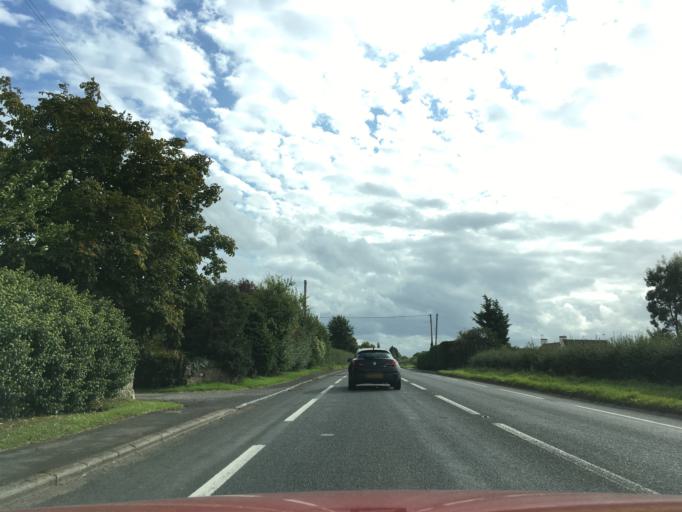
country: GB
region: England
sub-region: South Gloucestershire
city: Falfield
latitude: 51.6449
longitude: -2.4553
